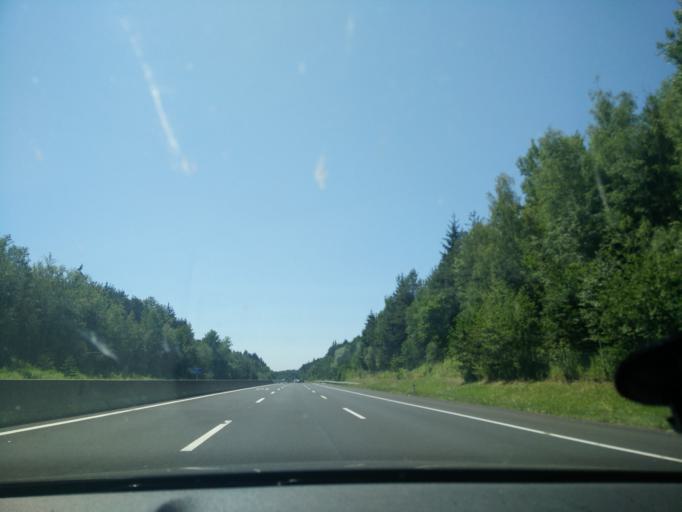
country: AT
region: Styria
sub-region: Politischer Bezirk Hartberg-Fuerstenfeld
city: Bad Waltersdorf
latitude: 47.1506
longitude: 15.9978
